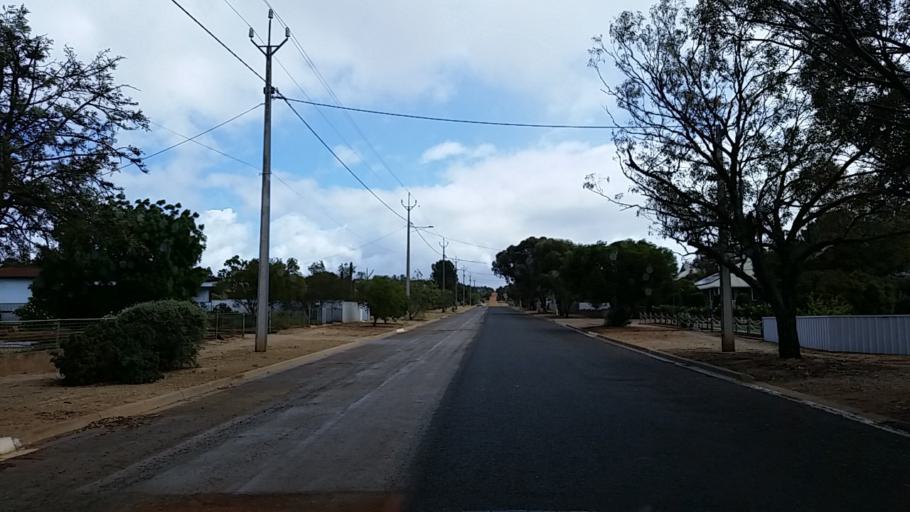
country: AU
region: South Australia
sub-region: Peterborough
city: Peterborough
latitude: -32.9683
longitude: 138.8317
